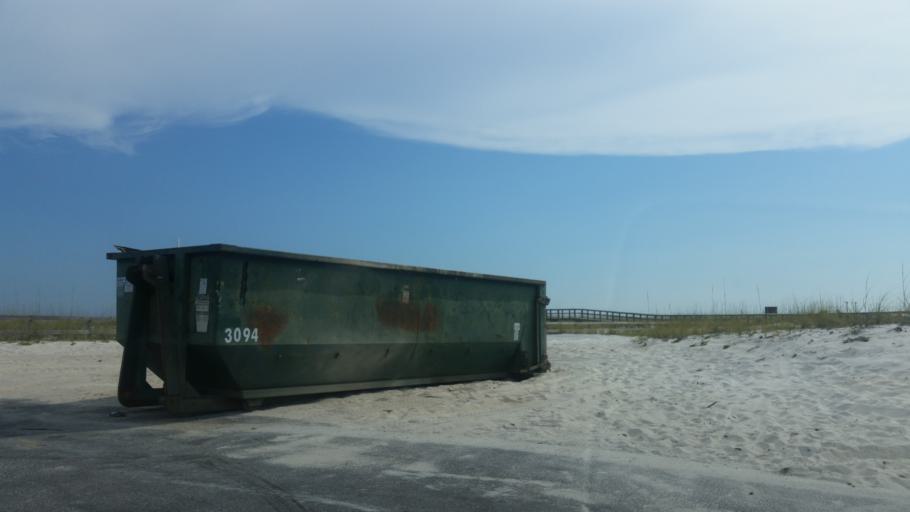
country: US
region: Florida
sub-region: Santa Rosa County
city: Tiger Point
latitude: 30.3477
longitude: -87.0567
